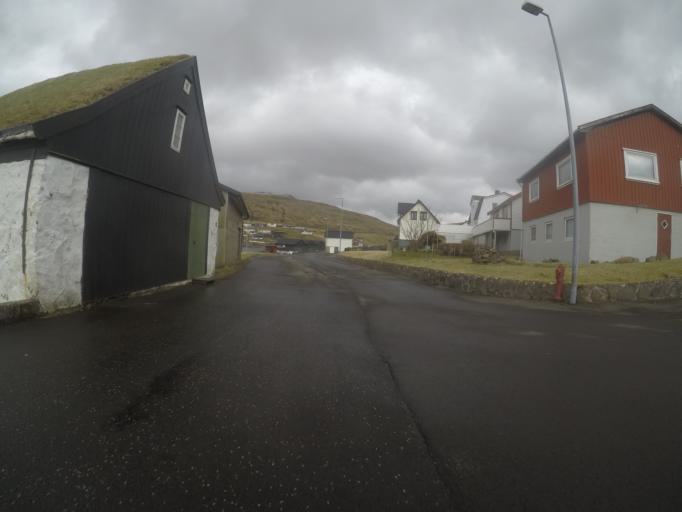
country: FO
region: Vagar
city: Midvagur
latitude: 62.0505
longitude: -7.1508
